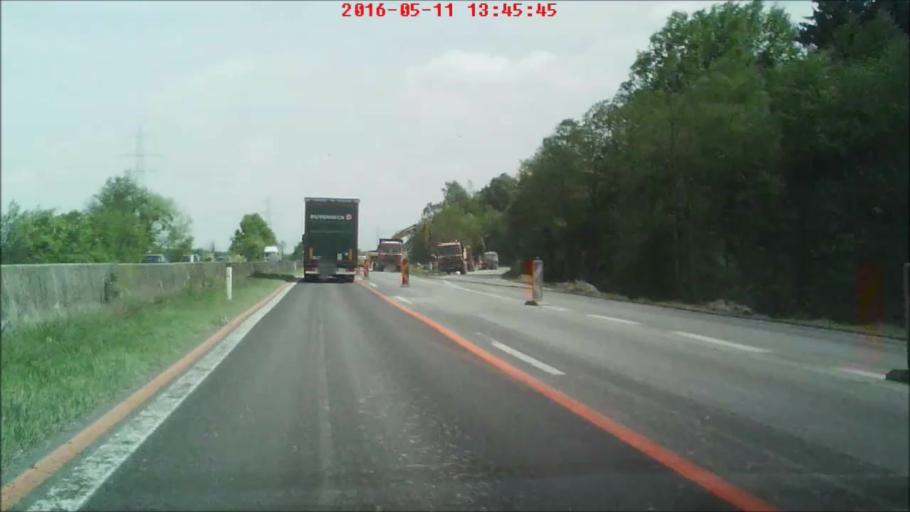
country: AT
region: Upper Austria
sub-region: Politischer Bezirk Vocklabruck
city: Wolfsegg am Hausruck
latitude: 48.2156
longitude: 13.6240
